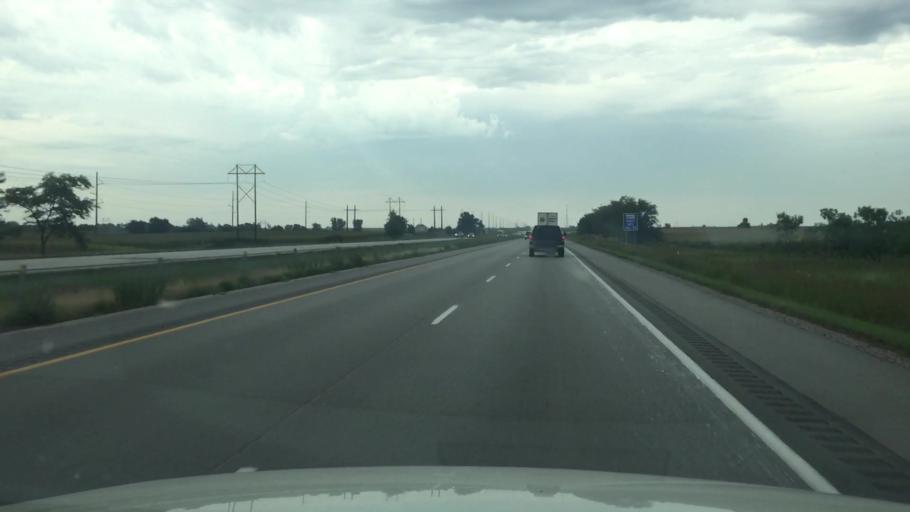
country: US
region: Iowa
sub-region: Story County
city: Huxley
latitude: 41.8461
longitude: -93.5713
